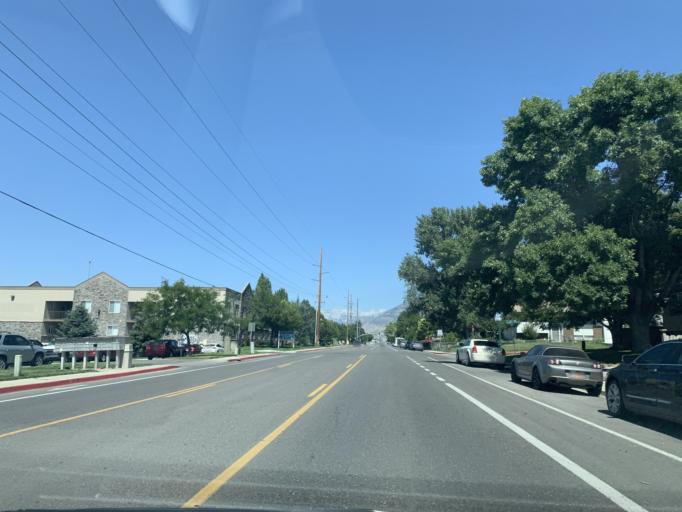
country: US
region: Utah
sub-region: Utah County
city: Orem
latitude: 40.2870
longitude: -111.7241
